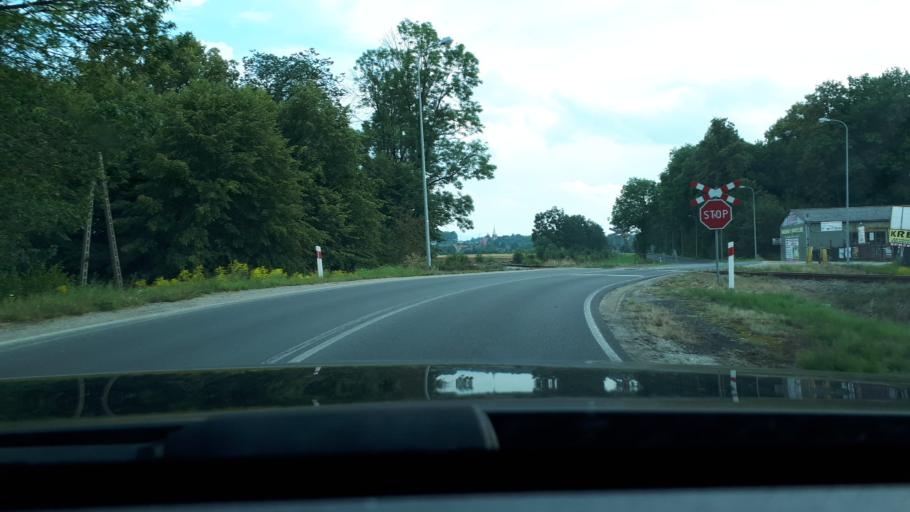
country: PL
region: Lower Silesian Voivodeship
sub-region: Powiat lubanski
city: Luban
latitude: 51.0762
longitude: 15.2954
